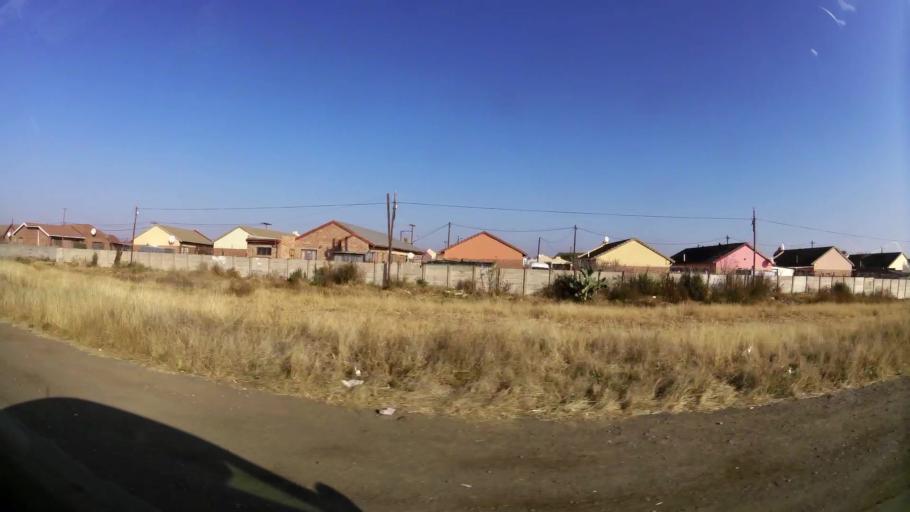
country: ZA
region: Orange Free State
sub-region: Mangaung Metropolitan Municipality
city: Bloemfontein
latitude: -29.1490
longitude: 26.2655
